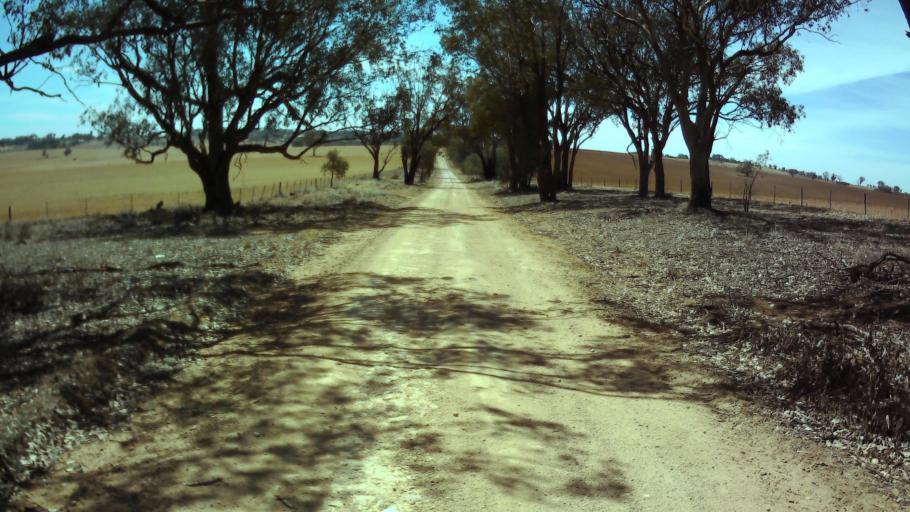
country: AU
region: New South Wales
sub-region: Weddin
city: Grenfell
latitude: -33.9432
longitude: 148.1455
